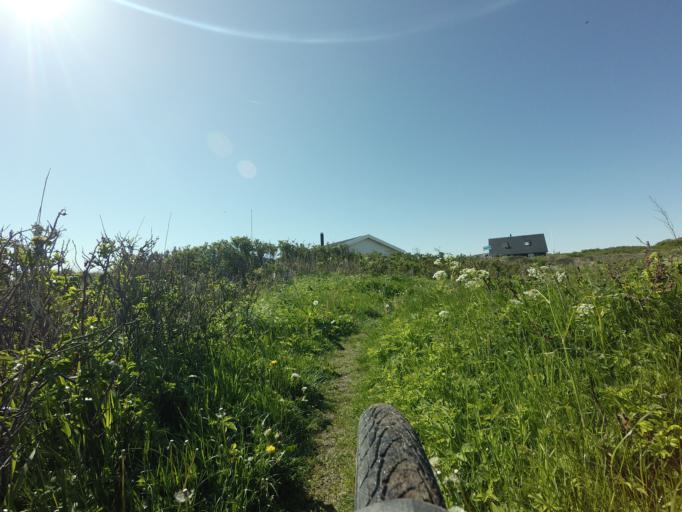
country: DK
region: North Denmark
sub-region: Jammerbugt Kommune
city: Pandrup
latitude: 57.3542
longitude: 9.6948
